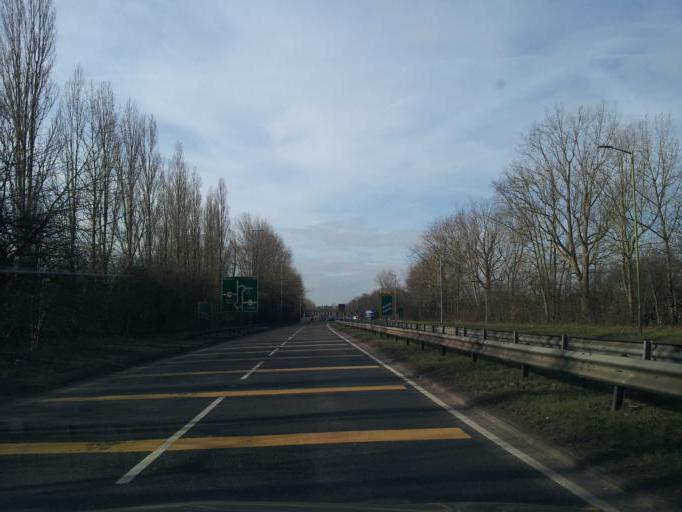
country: GB
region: England
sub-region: Hertfordshire
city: Hatfield
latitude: 51.7449
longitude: -0.2626
